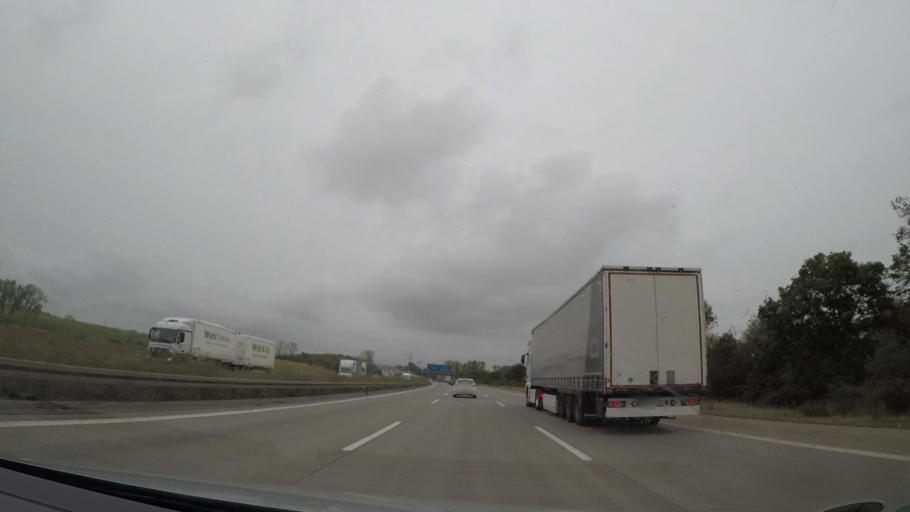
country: DE
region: Saxony-Anhalt
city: Hohenwarsleben
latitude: 52.1639
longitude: 11.5196
